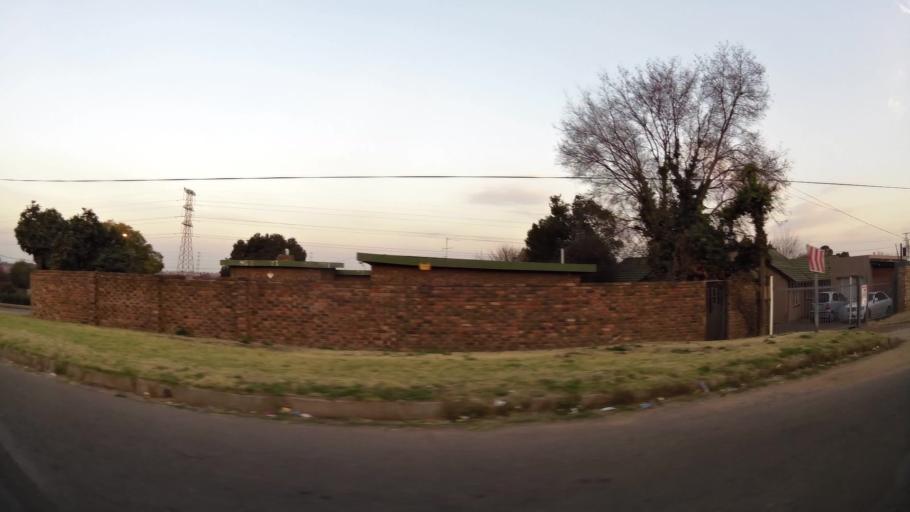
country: ZA
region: Gauteng
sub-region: Ekurhuleni Metropolitan Municipality
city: Tembisa
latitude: -26.0617
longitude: 28.2385
